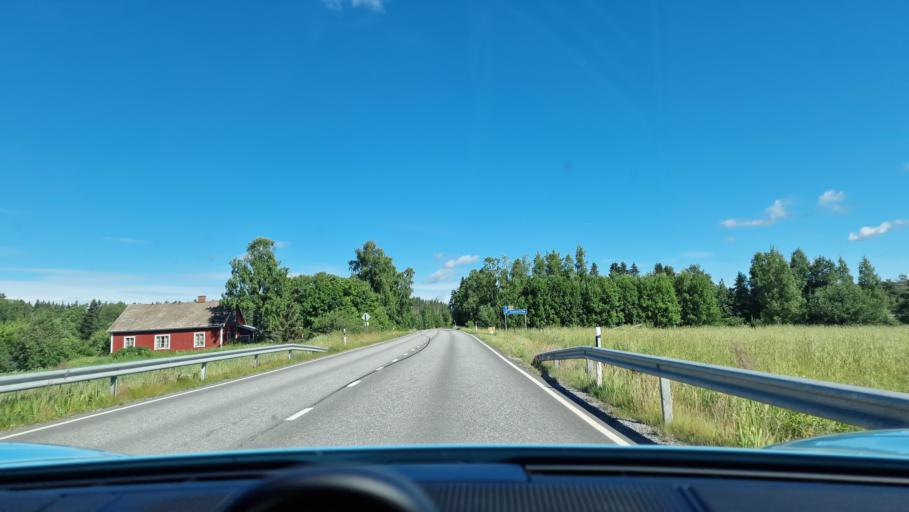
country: FI
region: Pirkanmaa
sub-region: Tampere
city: Sahalahti
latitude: 61.5522
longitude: 24.3146
